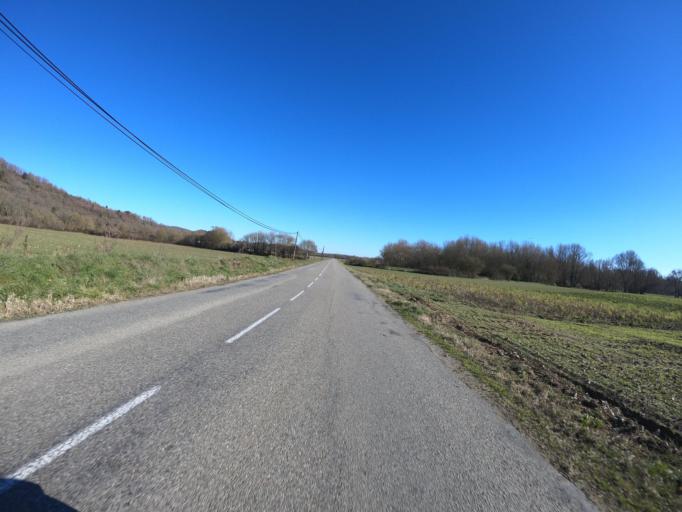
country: FR
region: Midi-Pyrenees
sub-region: Departement de l'Ariege
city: Mirepoix
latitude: 43.0947
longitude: 1.8481
